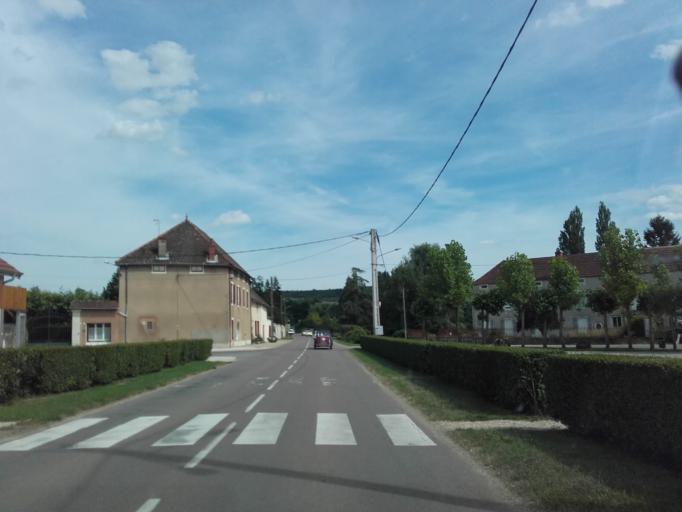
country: FR
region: Bourgogne
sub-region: Departement de Saone-et-Loire
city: Chagny
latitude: 46.9099
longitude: 4.7041
